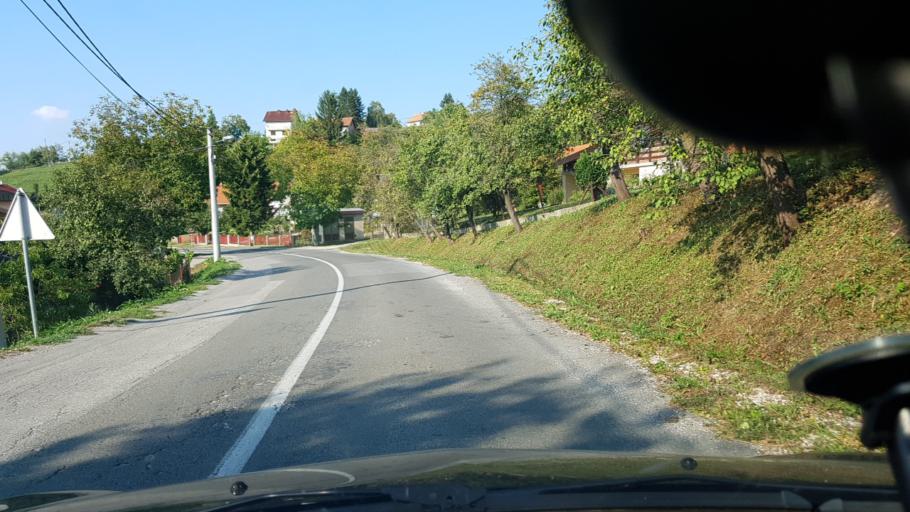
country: HR
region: Zagrebacka
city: Bregana
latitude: 45.9013
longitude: 15.6847
